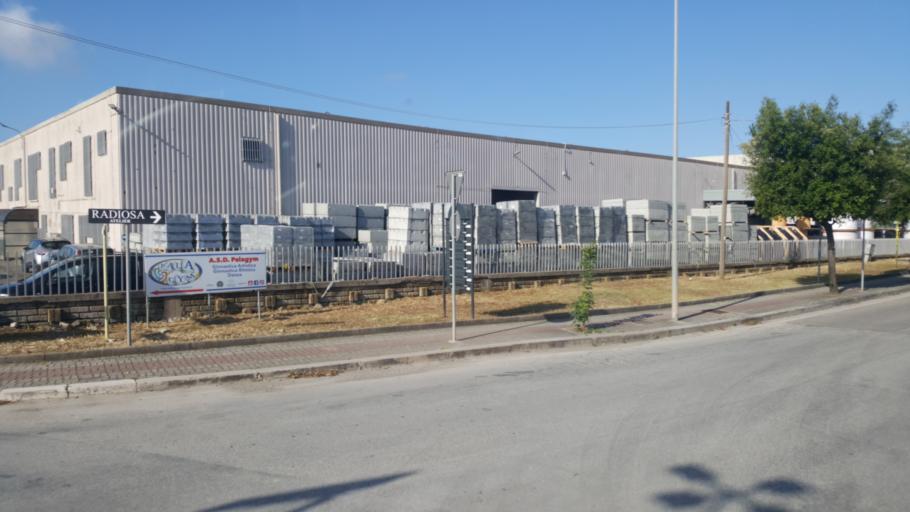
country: IT
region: Latium
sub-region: Provincia di Latina
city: Aprilia
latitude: 41.5786
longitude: 12.6468
